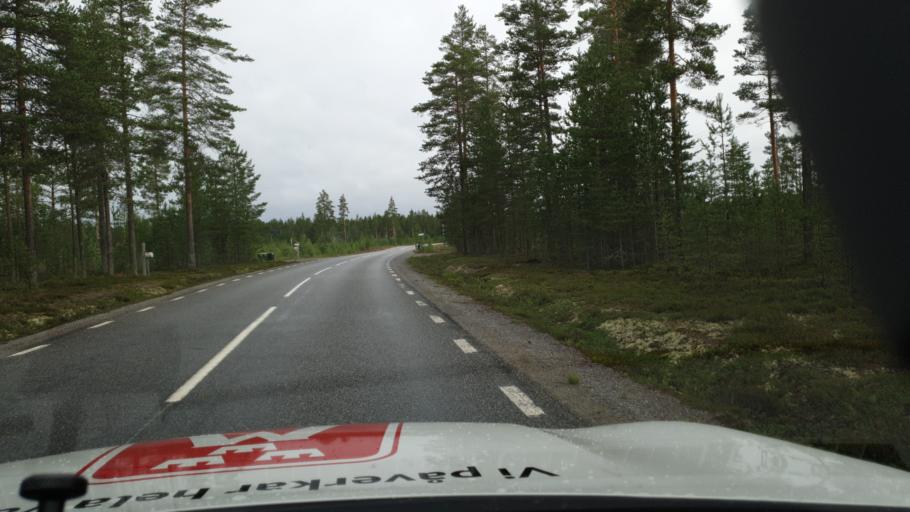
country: SE
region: Vaesterbotten
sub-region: Umea Kommun
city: Saevar
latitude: 63.9824
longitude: 20.5045
